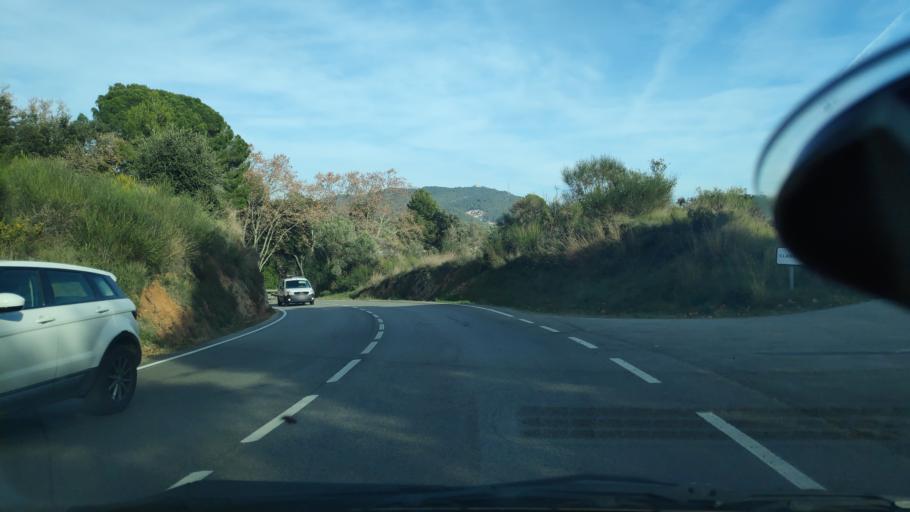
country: ES
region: Catalonia
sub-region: Provincia de Barcelona
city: Castellar del Valles
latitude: 41.6087
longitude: 2.0717
